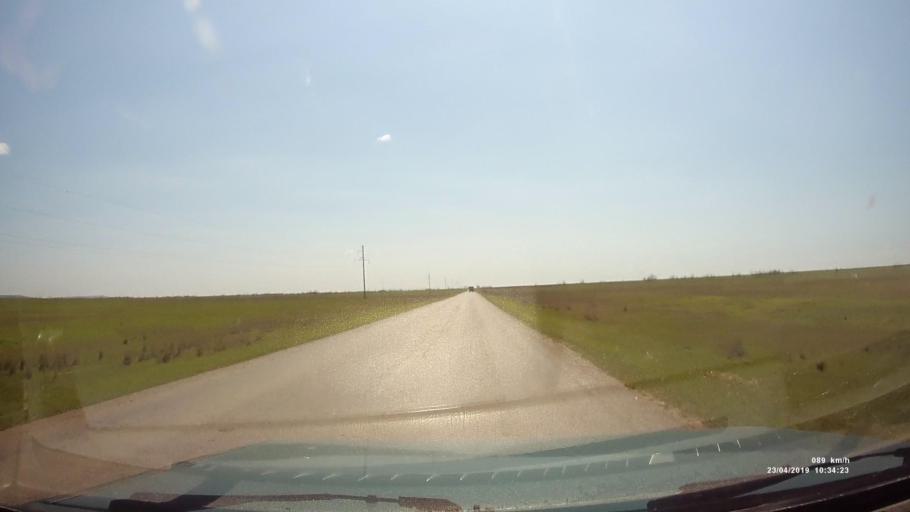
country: RU
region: Kalmykiya
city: Yashalta
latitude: 46.5645
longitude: 42.6096
